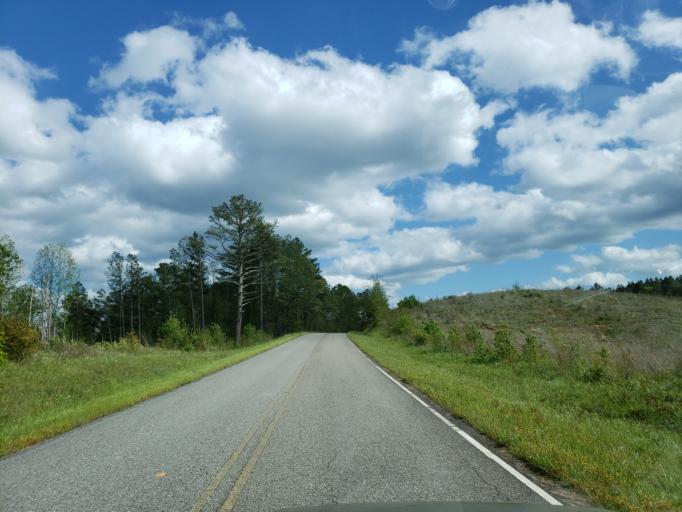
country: US
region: Georgia
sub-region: Haralson County
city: Tallapoosa
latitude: 33.7107
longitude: -85.3819
